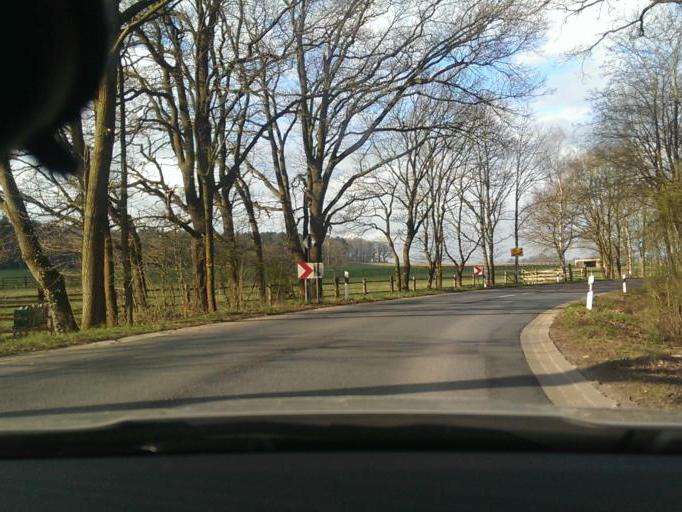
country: DE
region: Lower Saxony
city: Lindwedel
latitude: 52.5734
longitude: 9.6368
